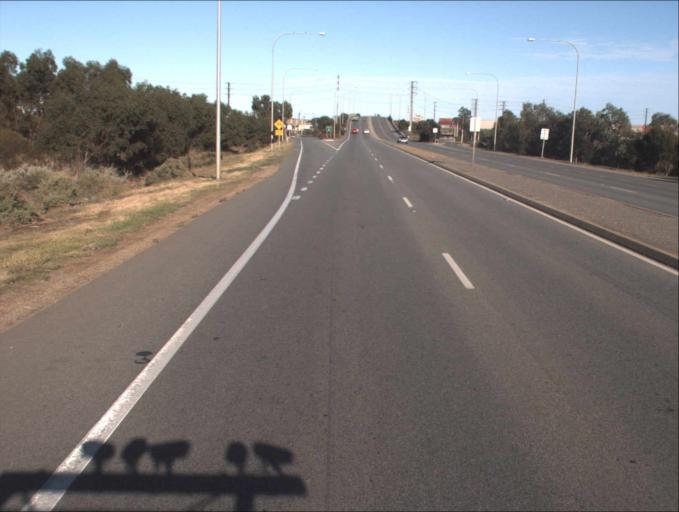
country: AU
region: South Australia
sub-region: Port Adelaide Enfield
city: Alberton
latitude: -34.8369
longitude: 138.5259
